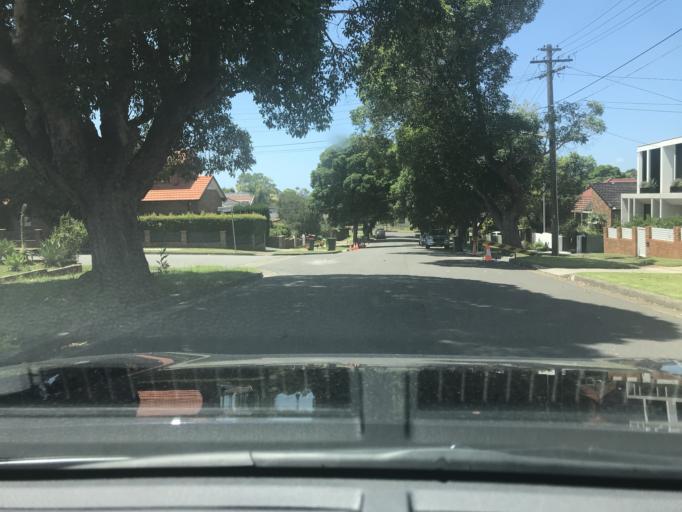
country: AU
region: New South Wales
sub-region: Canada Bay
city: Concord
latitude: -33.8594
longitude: 151.1010
